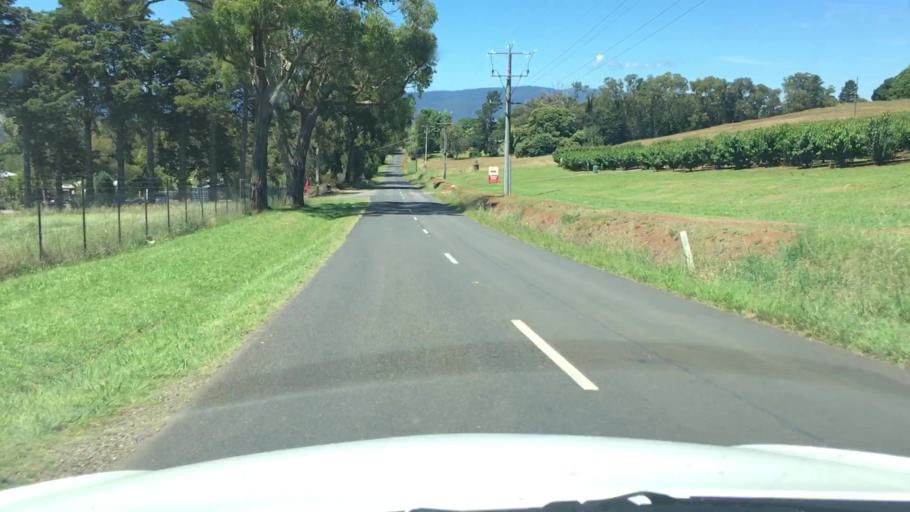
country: AU
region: Victoria
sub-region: Yarra Ranges
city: Mount Evelyn
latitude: -37.7948
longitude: 145.4285
